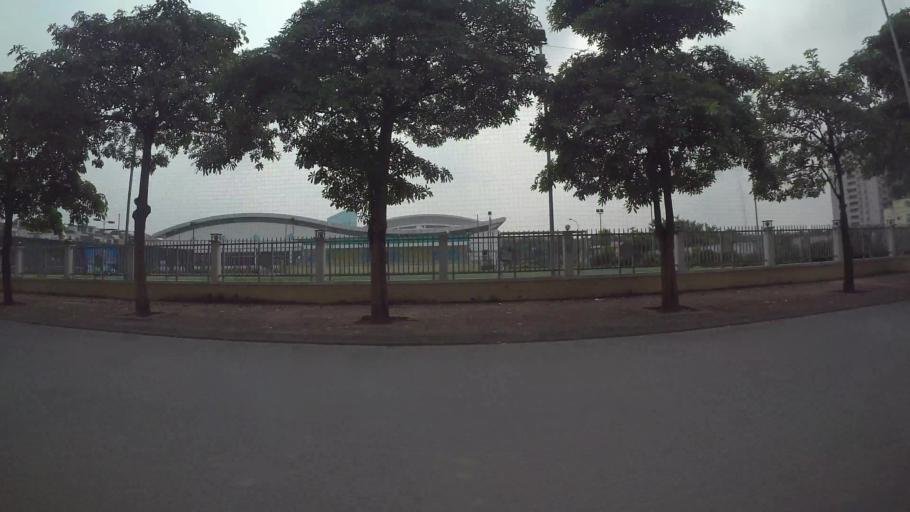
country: VN
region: Ha Noi
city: Trau Quy
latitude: 21.0567
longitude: 105.9083
